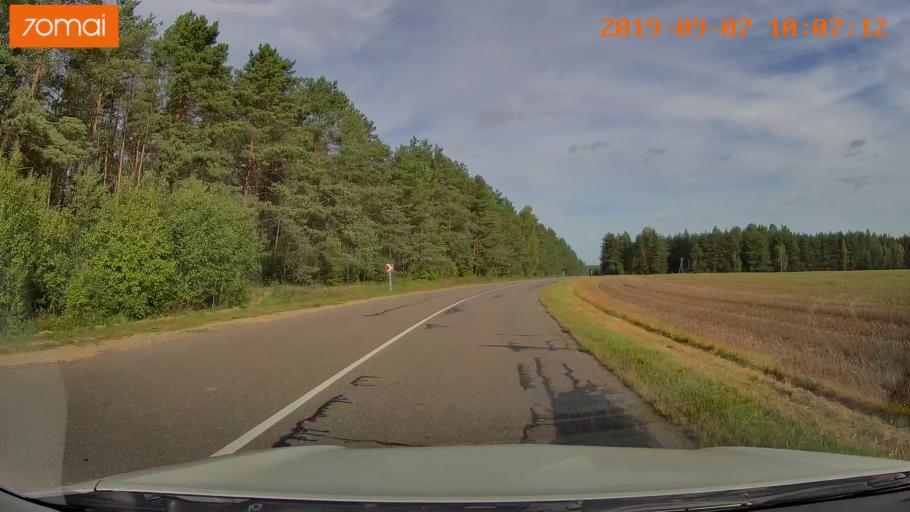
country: BY
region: Grodnenskaya
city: Voranava
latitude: 54.0719
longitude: 25.3967
